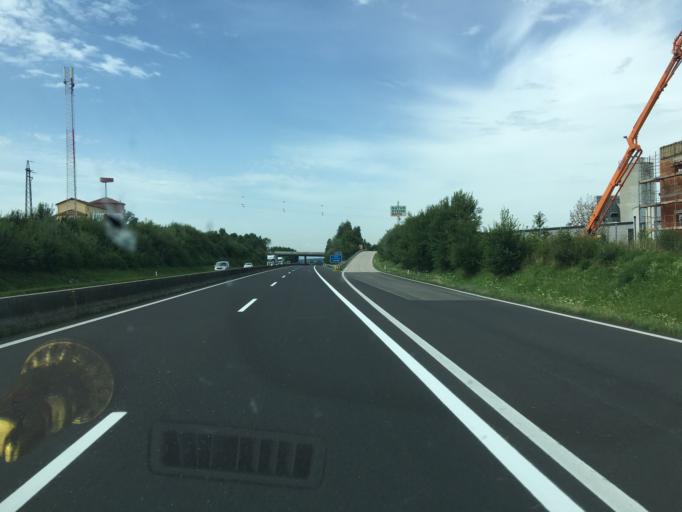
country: AT
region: Upper Austria
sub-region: Wels-Land
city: Sattledt
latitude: 48.0153
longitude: 14.0686
